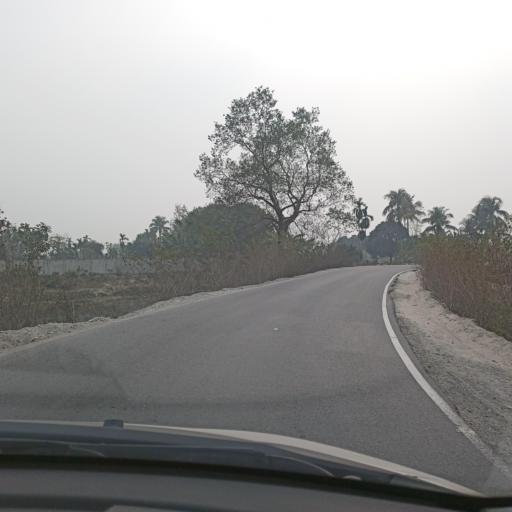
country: IN
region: West Bengal
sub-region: Jalpaiguri
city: Odlabari
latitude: 26.7454
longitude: 88.5805
